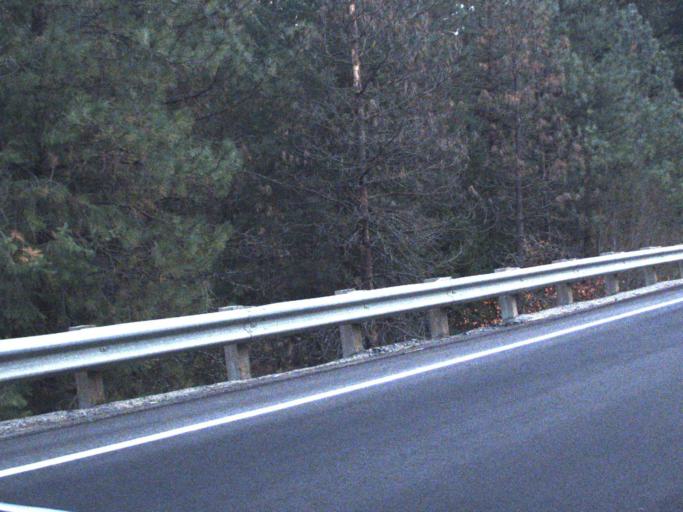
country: US
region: Washington
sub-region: Lincoln County
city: Davenport
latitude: 48.0279
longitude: -118.2328
